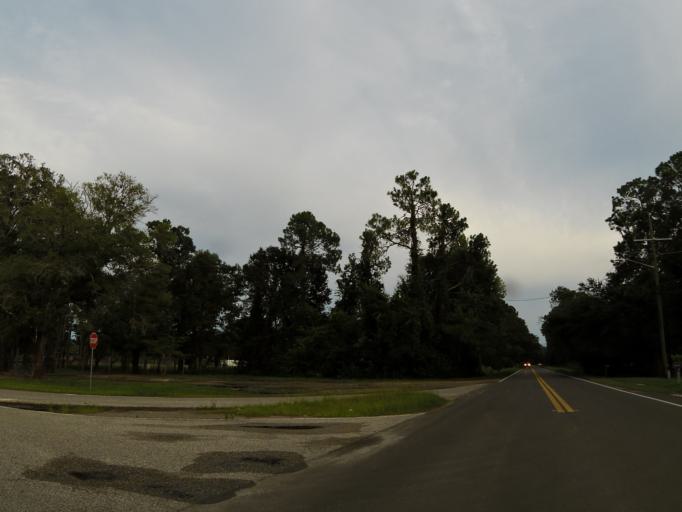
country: US
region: Florida
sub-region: Duval County
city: Jacksonville
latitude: 30.3941
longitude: -81.7519
